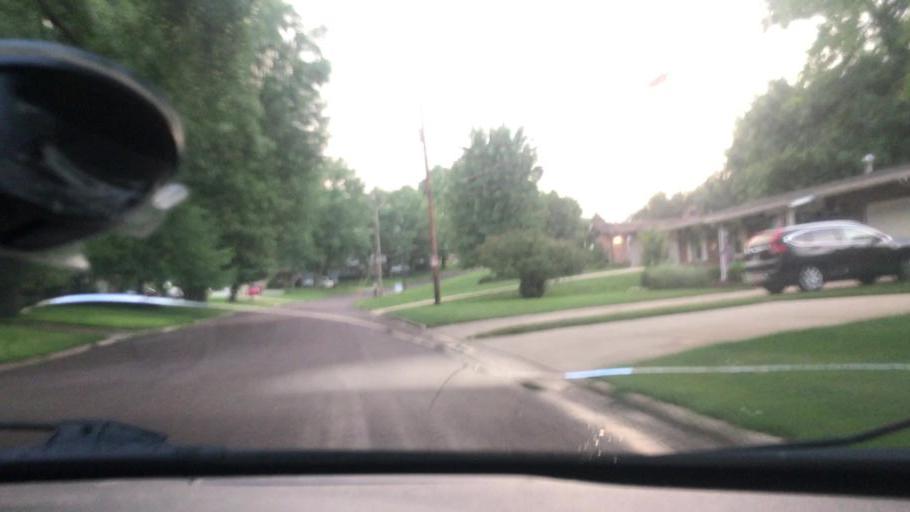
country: US
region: Illinois
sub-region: Tazewell County
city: Pekin
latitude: 40.5527
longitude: -89.6140
